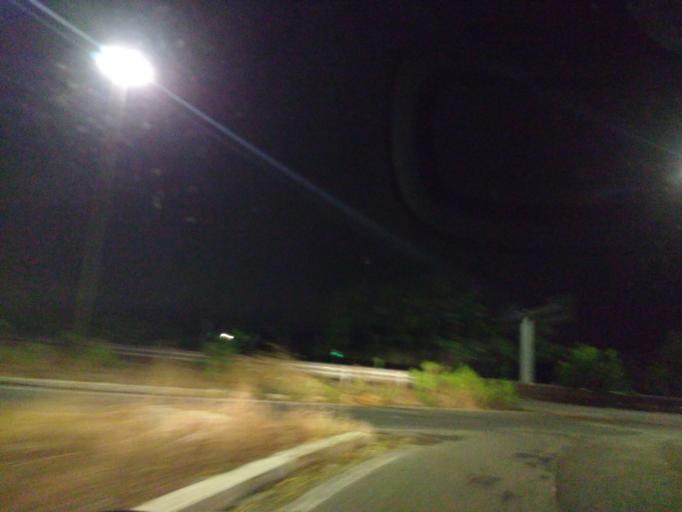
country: IT
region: Latium
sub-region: Citta metropolitana di Roma Capitale
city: Vitinia
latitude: 41.7889
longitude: 12.4249
